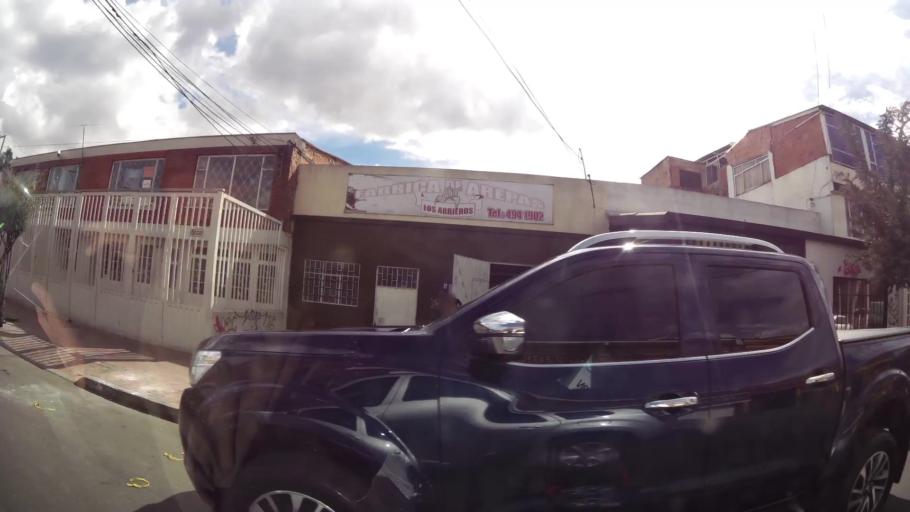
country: CO
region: Bogota D.C.
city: Bogota
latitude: 4.6168
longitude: -74.1328
